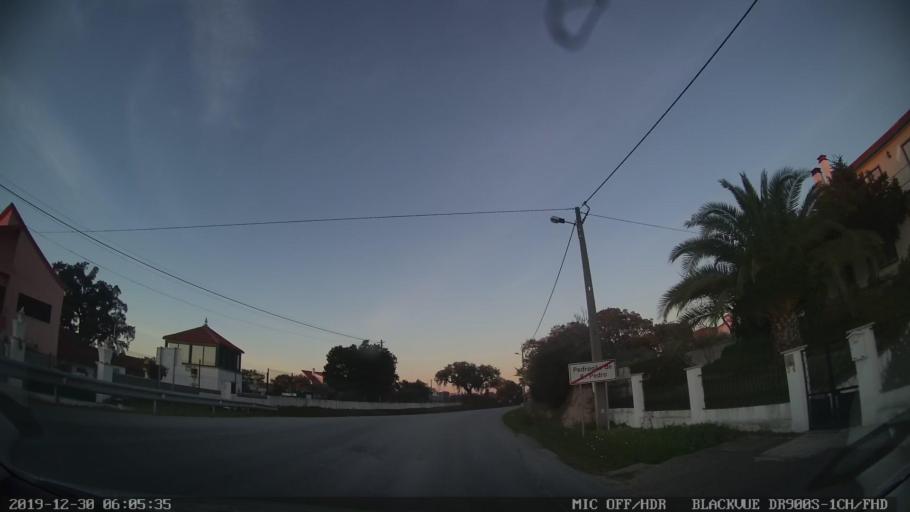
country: PT
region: Castelo Branco
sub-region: Penamacor
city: Penamacor
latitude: 40.0916
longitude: -7.2365
